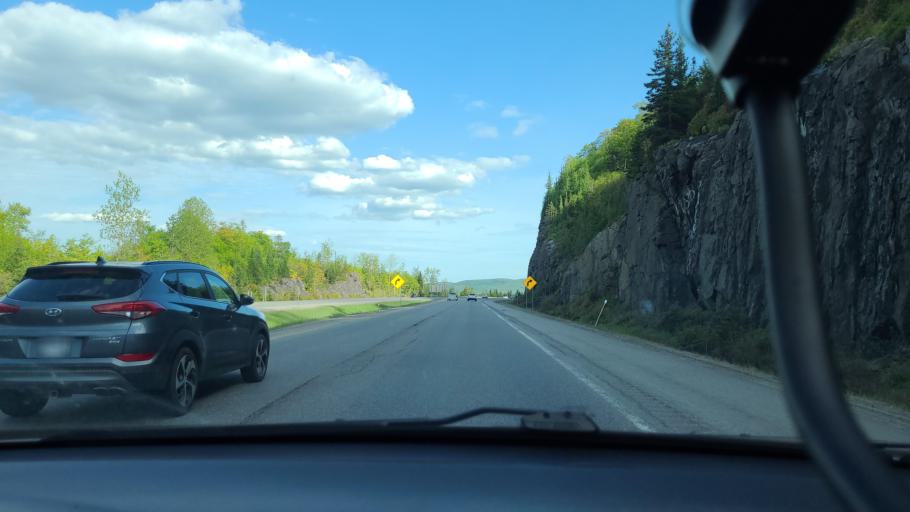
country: CA
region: Quebec
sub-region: Laurentides
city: Sainte-Adele
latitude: 45.9727
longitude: -74.1561
